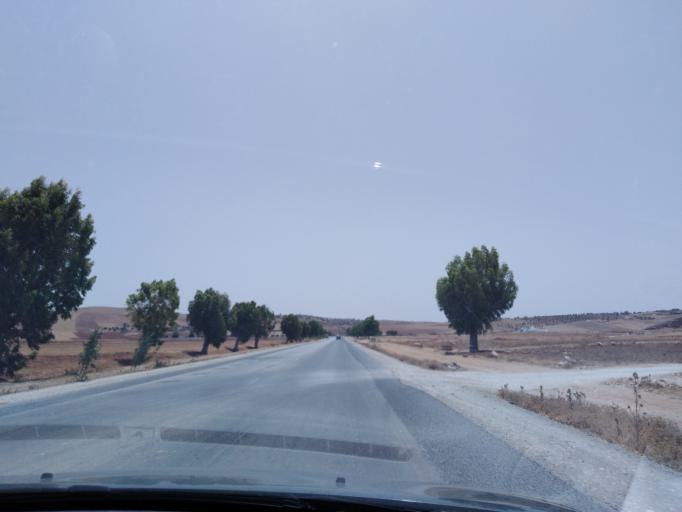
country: MA
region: Doukkala-Abda
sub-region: Safi
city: Youssoufia
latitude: 32.1655
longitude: -8.8581
